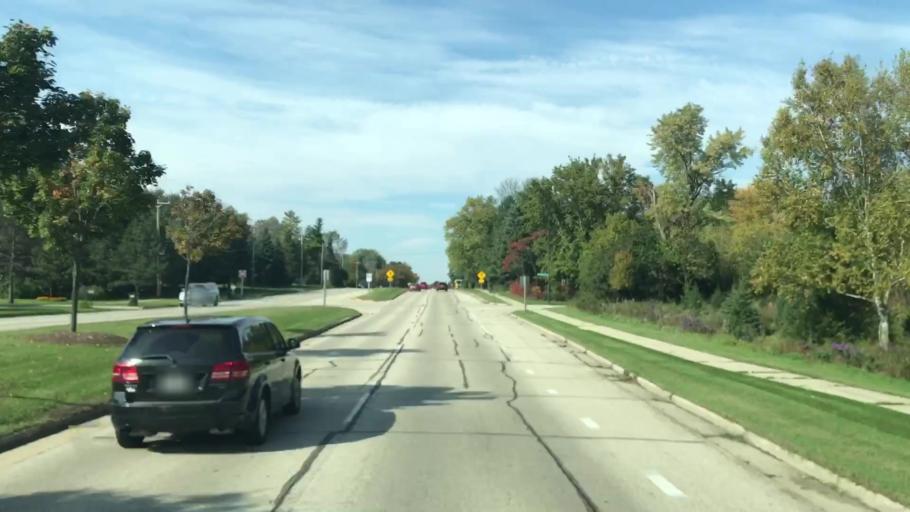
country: US
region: Wisconsin
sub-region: Ozaukee County
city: Thiensville
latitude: 43.2216
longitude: -87.9498
